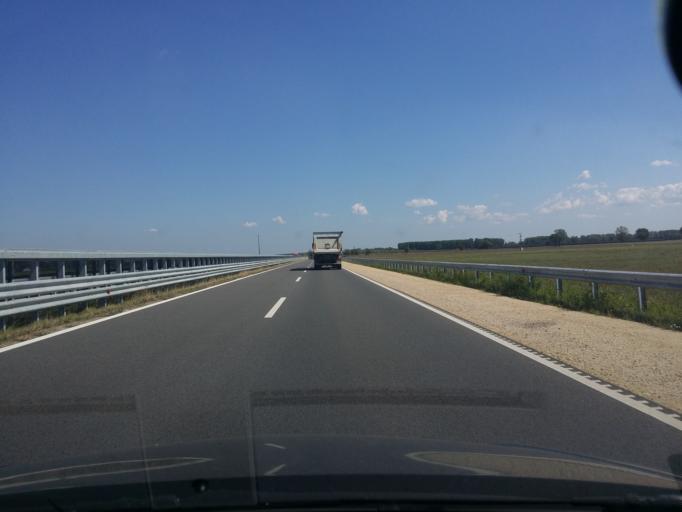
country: HU
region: Gyor-Moson-Sopron
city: Farad
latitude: 47.5258
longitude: 17.2033
